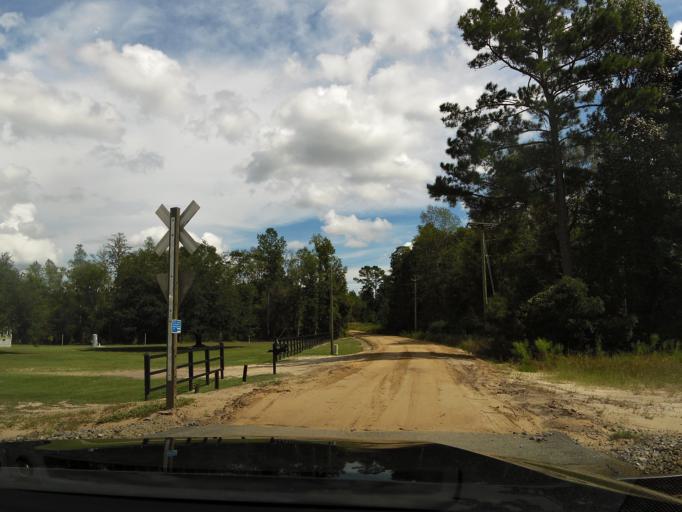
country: US
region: Georgia
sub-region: Brantley County
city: Nahunta
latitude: 31.0937
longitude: -82.0091
